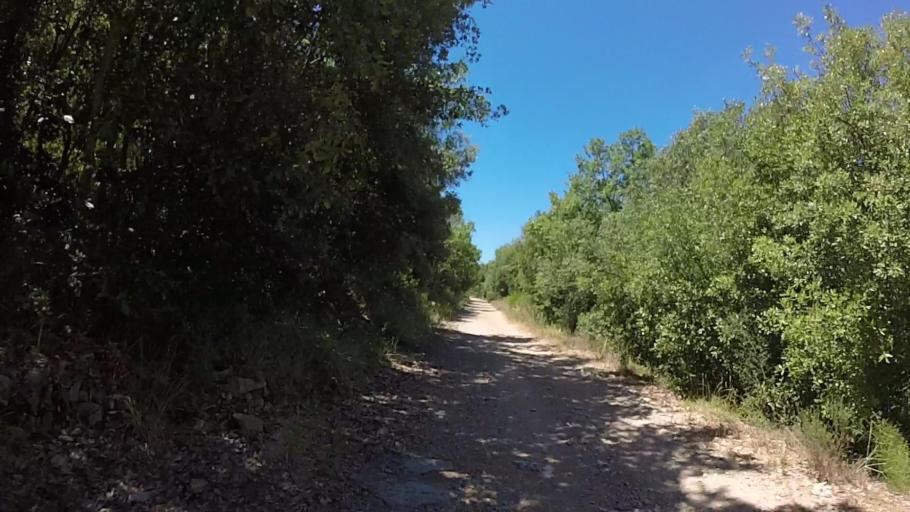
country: FR
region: Provence-Alpes-Cote d'Azur
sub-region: Departement des Alpes-Maritimes
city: Valbonne
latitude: 43.6336
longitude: 7.0454
